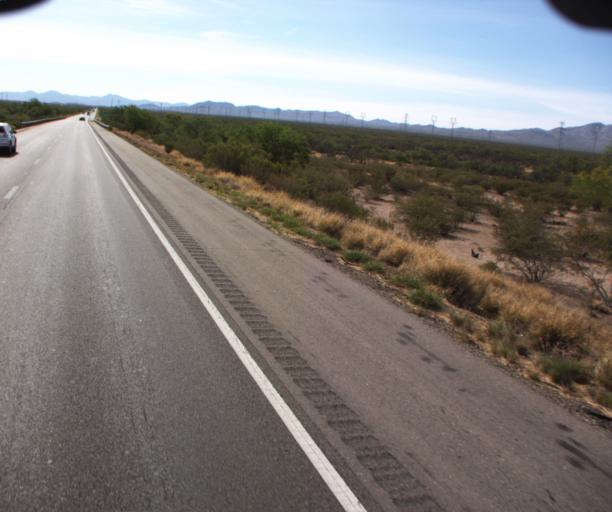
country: US
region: Arizona
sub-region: Pima County
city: Vail
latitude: 32.0463
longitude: -110.7496
